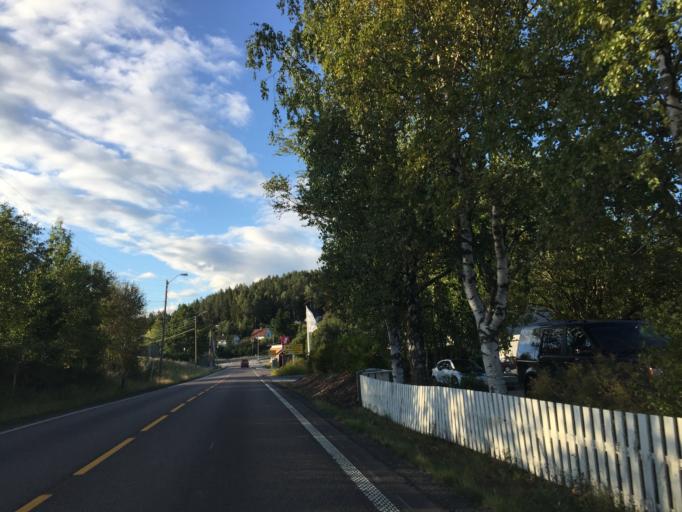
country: NO
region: Akershus
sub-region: Fet
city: Fetsund
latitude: 59.8805
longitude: 11.2202
